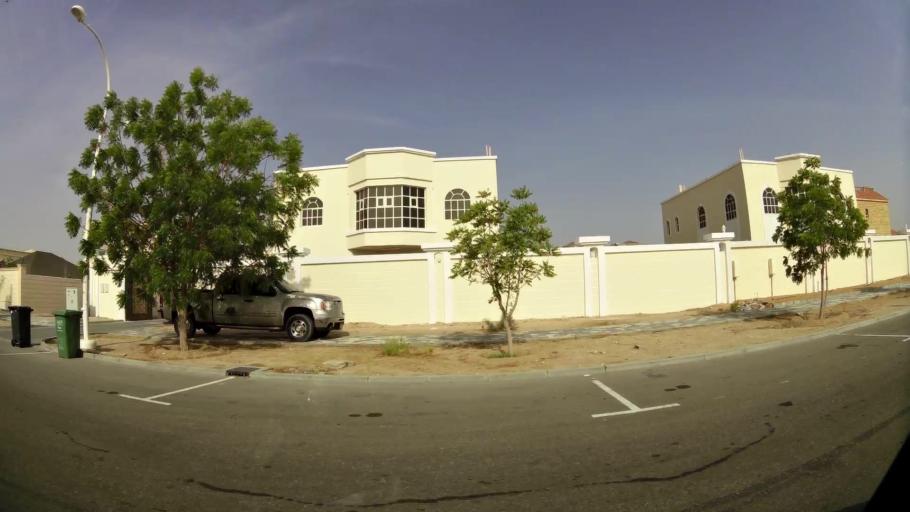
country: AE
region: Abu Dhabi
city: Al Ain
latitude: 24.1523
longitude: 55.7195
